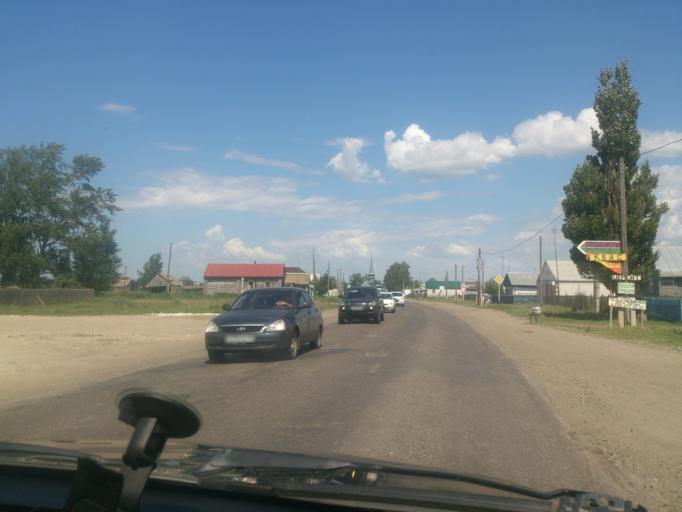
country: RU
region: Ulyanovsk
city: Cherdakly
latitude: 54.4281
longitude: 48.8948
